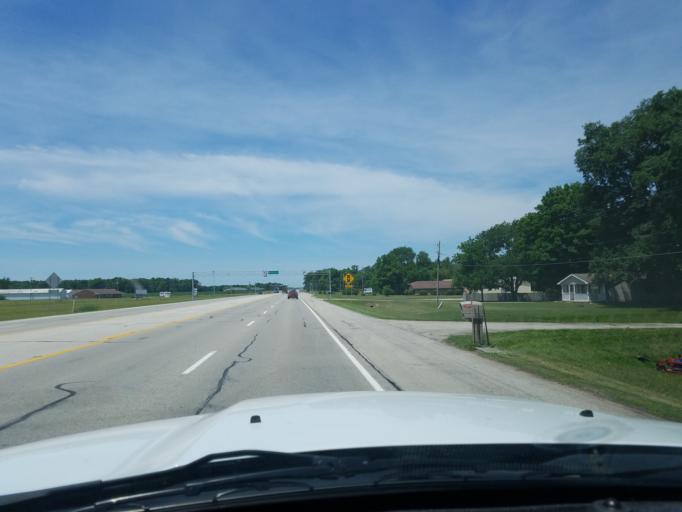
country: US
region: Indiana
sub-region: Delaware County
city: Daleville
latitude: 40.1134
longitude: -85.5331
